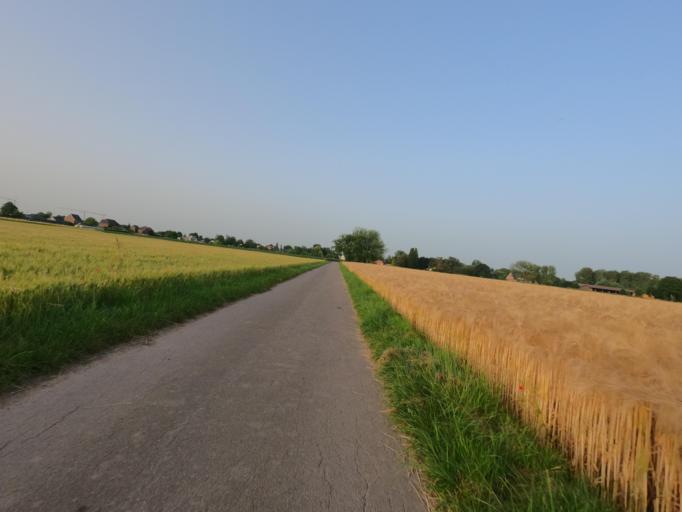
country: DE
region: North Rhine-Westphalia
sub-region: Regierungsbezirk Koln
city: Wassenberg
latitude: 51.0937
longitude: 6.1485
